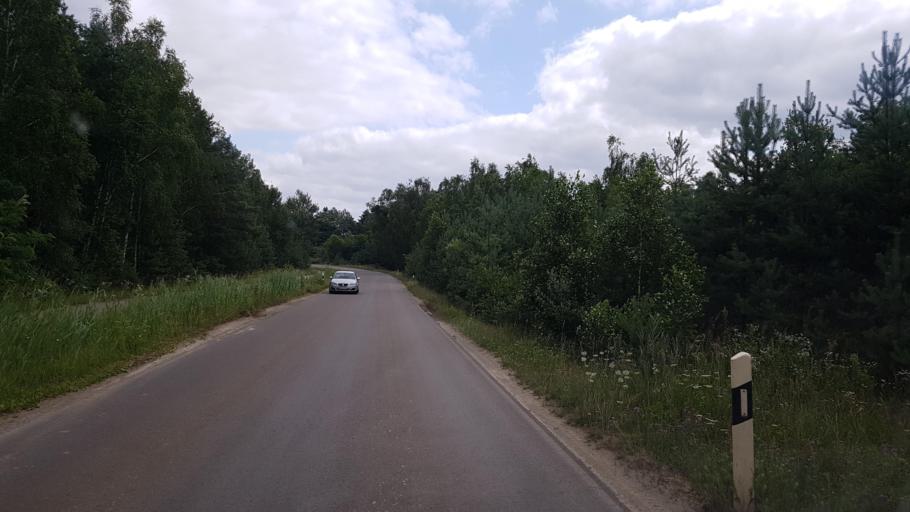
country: DE
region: Brandenburg
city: Altdobern
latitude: 51.6428
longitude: 14.0953
